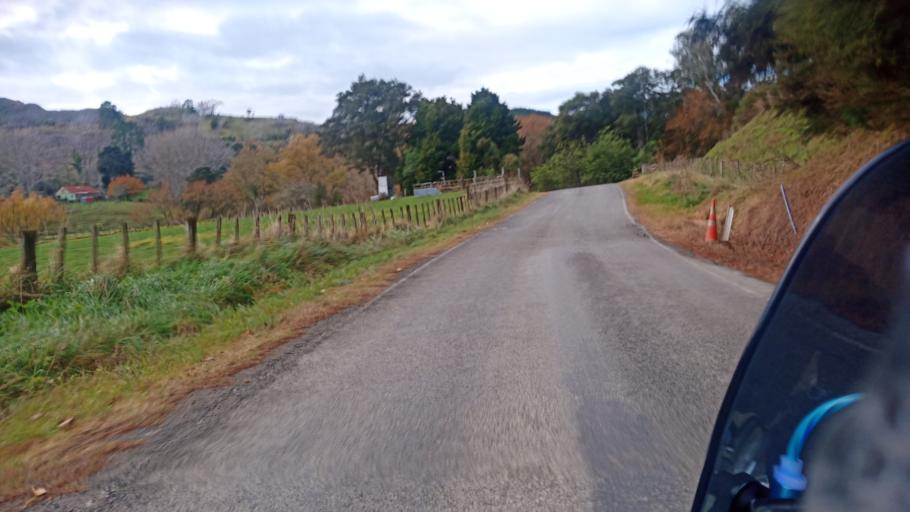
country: NZ
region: Gisborne
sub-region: Gisborne District
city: Gisborne
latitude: -38.4098
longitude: 177.9468
